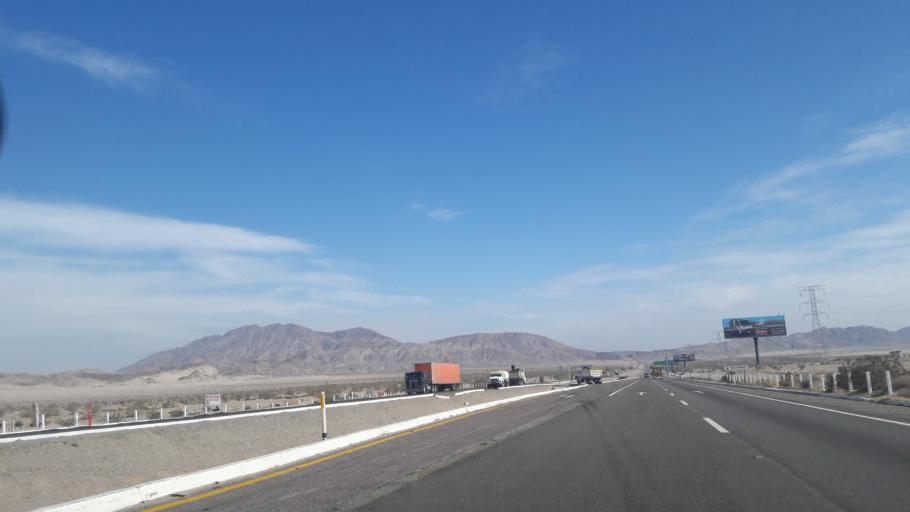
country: MX
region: Baja California
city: Progreso
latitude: 32.5718
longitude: -115.7959
